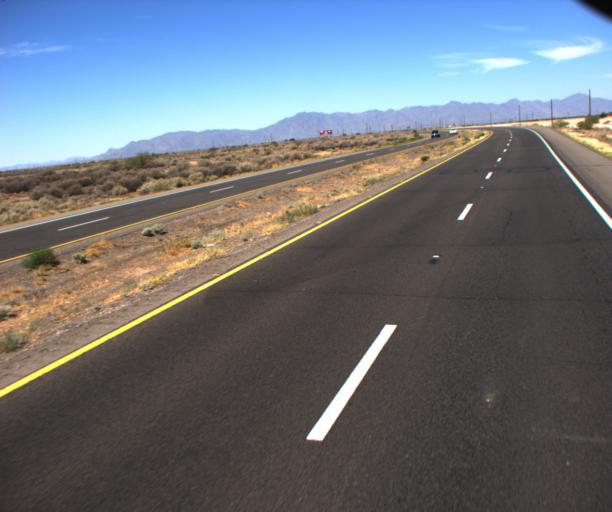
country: US
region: Arizona
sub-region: Maricopa County
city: Sun Lakes
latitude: 33.2522
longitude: -111.9699
